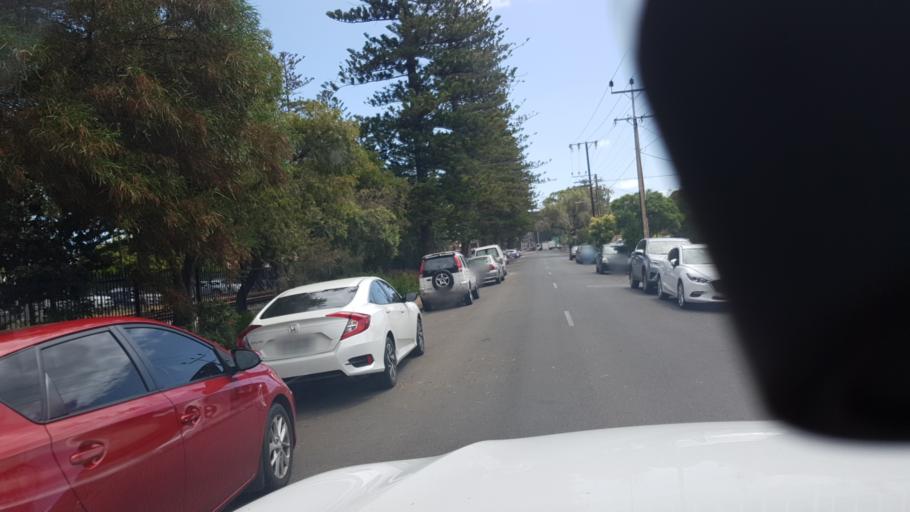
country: AU
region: South Australia
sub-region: Holdfast Bay
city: Glenelg East
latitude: -34.9798
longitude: 138.5228
